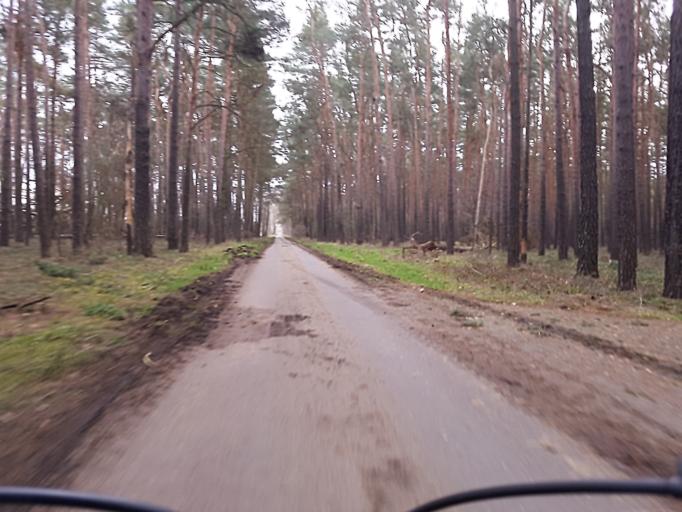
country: DE
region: Brandenburg
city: Schilda
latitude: 51.5740
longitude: 13.3821
